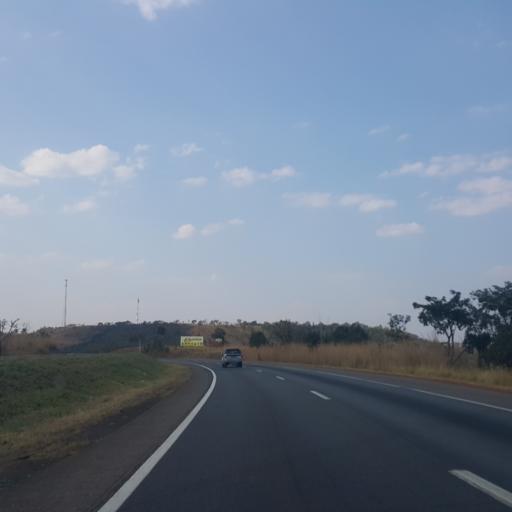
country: BR
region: Goias
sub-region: Abadiania
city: Abadiania
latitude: -16.1079
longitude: -48.5259
